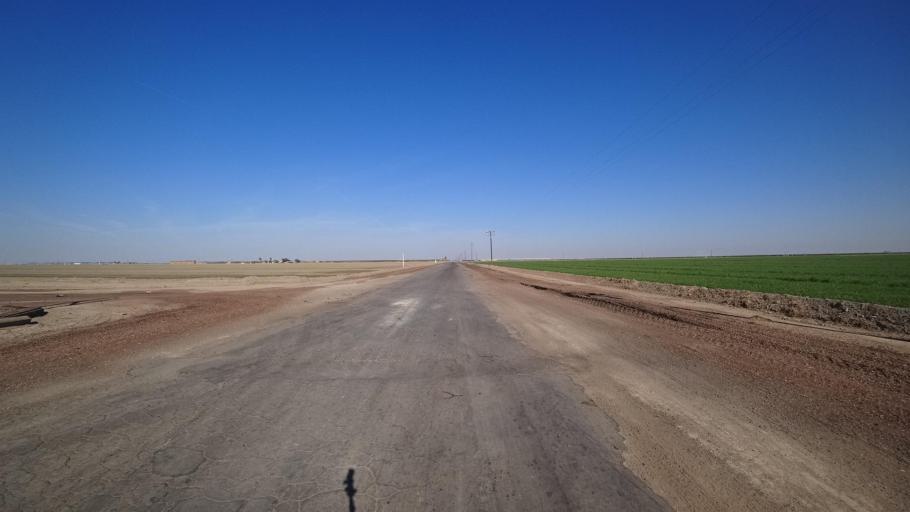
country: US
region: California
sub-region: Kern County
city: Wasco
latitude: 35.7184
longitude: -119.4194
